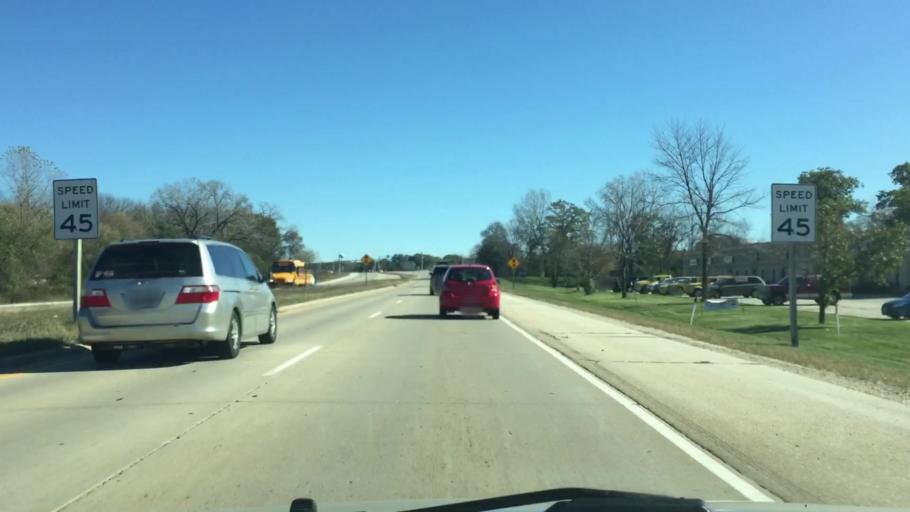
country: US
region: Wisconsin
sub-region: Waukesha County
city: Waukesha
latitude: 42.9770
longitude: -88.2332
